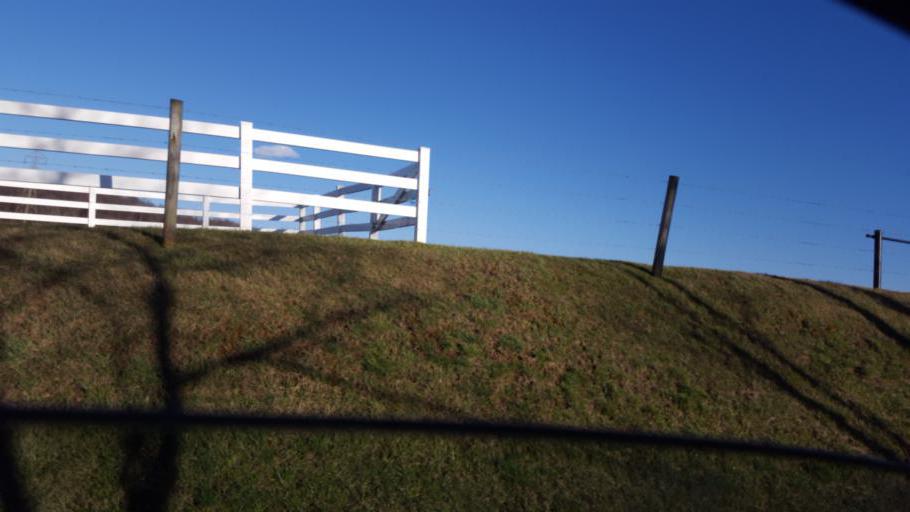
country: US
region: Ohio
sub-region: Tuscarawas County
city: Sugarcreek
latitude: 40.6048
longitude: -81.7612
